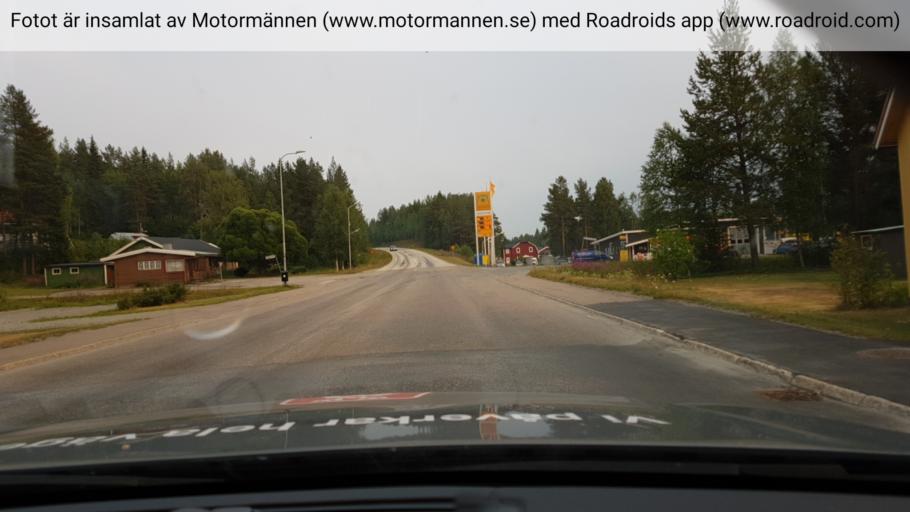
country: SE
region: Jaemtland
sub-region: Harjedalens Kommun
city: Sveg
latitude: 62.4225
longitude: 13.5359
